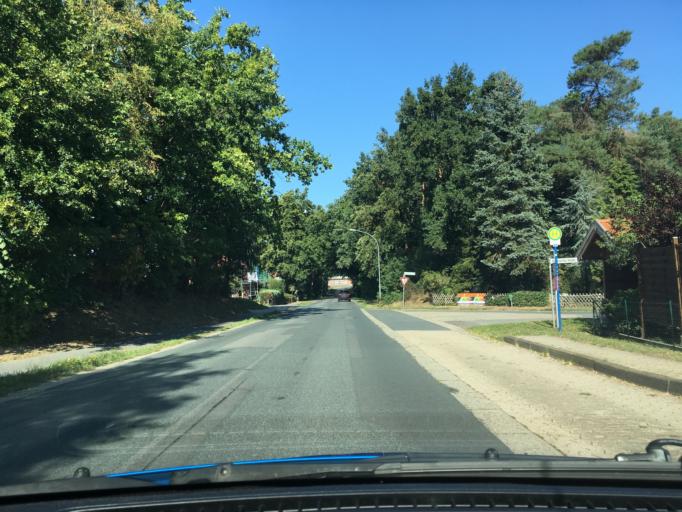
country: DE
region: Lower Saxony
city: Hermannsburg
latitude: 52.8593
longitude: 10.0518
